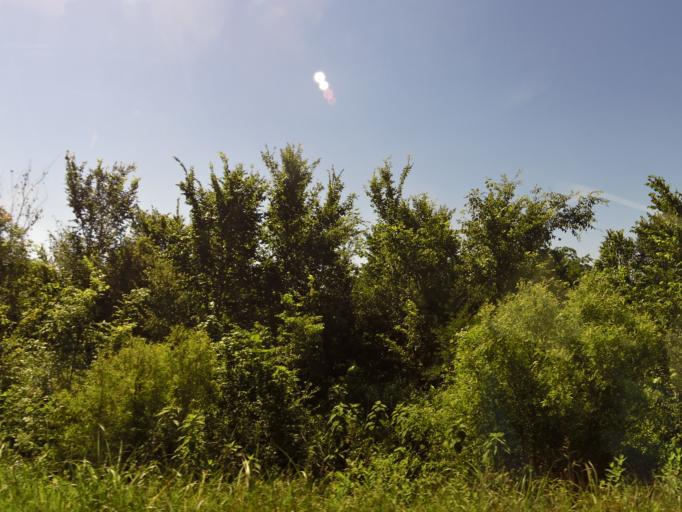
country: US
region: Missouri
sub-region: Dunklin County
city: Campbell
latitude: 36.4714
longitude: -90.1111
